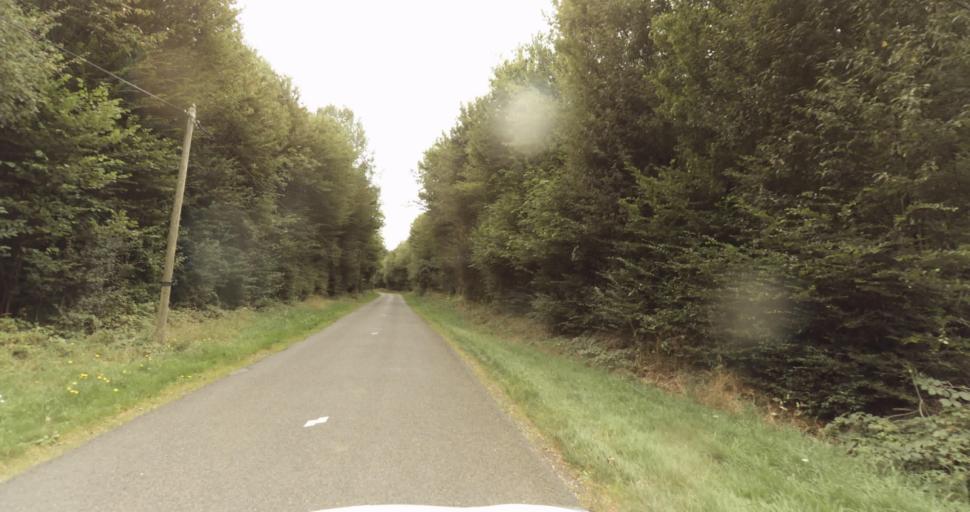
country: FR
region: Haute-Normandie
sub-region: Departement de l'Eure
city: La Madeleine-de-Nonancourt
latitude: 48.8279
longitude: 1.2283
